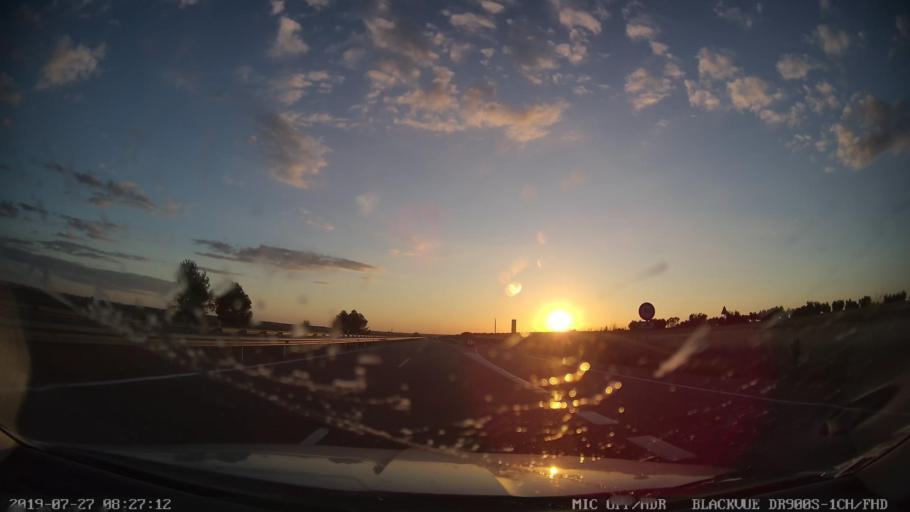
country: ES
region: Extremadura
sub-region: Provincia de Badajoz
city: Lobon
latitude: 38.8386
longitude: -6.6438
